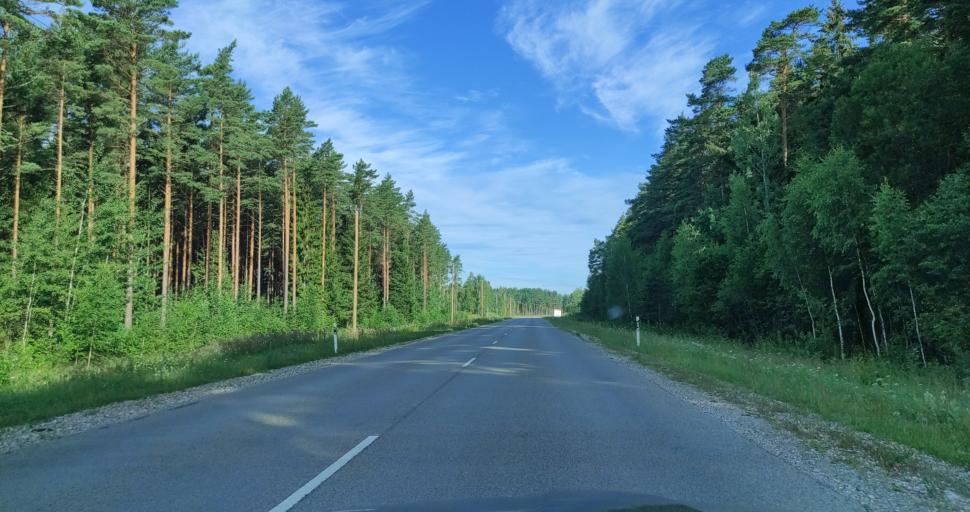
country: LV
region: Pavilostas
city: Pavilosta
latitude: 56.7933
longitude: 21.2403
